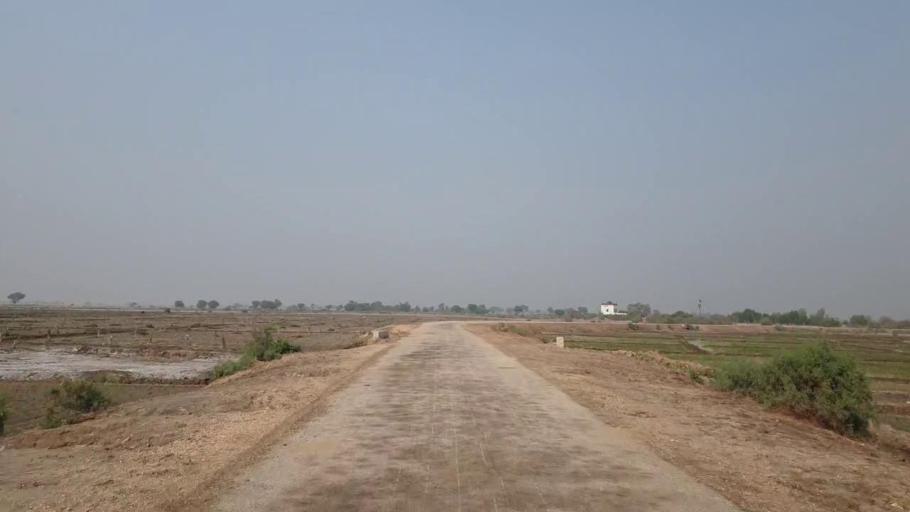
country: PK
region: Sindh
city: Bhan
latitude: 26.4866
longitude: 67.7002
